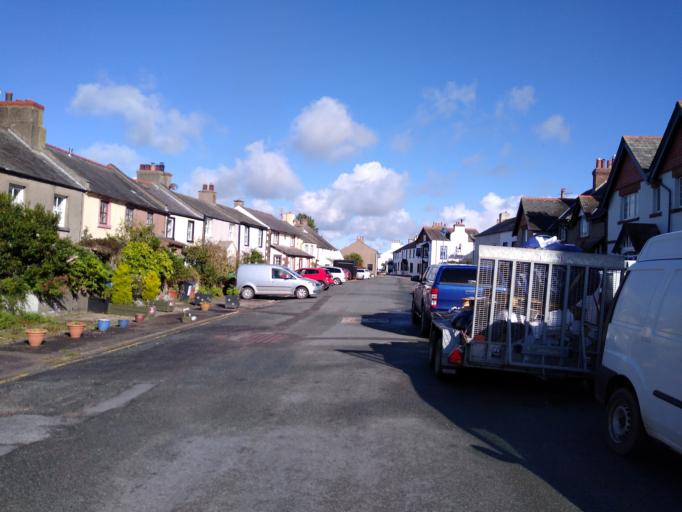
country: GB
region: England
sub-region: Cumbria
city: Seascale
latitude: 54.3538
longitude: -3.4107
